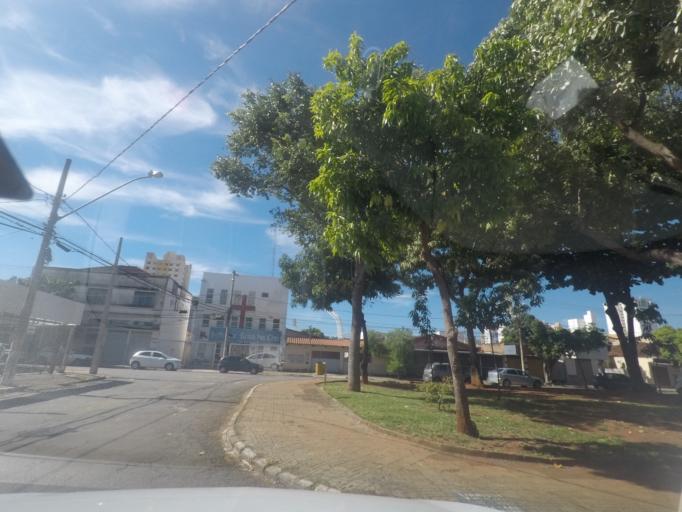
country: BR
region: Goias
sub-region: Goiania
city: Goiania
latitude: -16.6676
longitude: -49.2636
